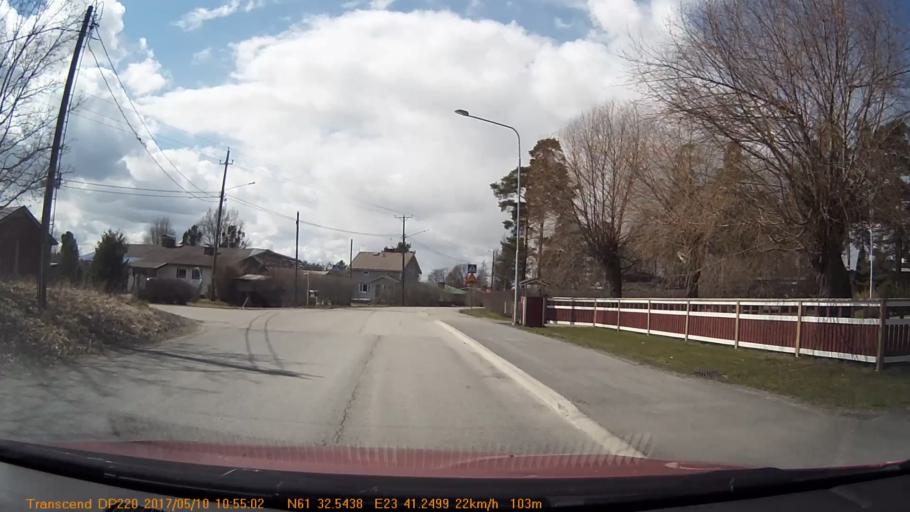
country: FI
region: Pirkanmaa
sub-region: Tampere
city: Yloejaervi
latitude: 61.5426
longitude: 23.6871
